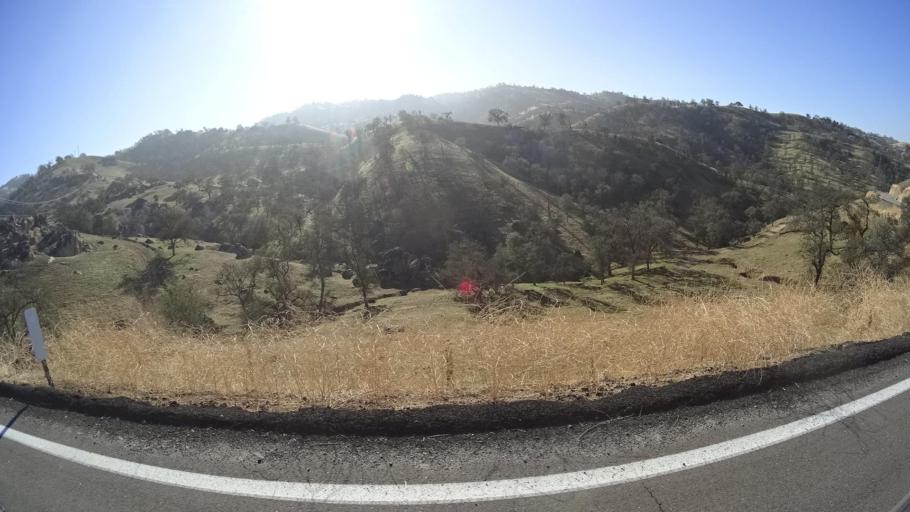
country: US
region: California
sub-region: Kern County
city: Alta Sierra
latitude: 35.7174
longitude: -118.8107
